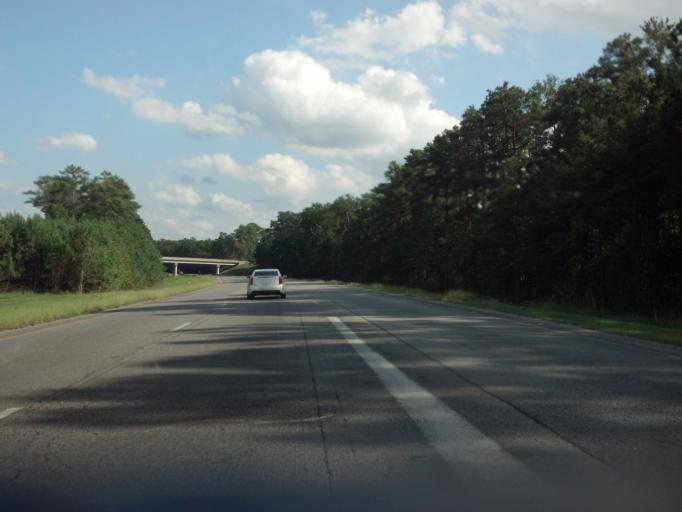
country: US
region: North Carolina
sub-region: Nash County
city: Rocky Mount
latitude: 35.9425
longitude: -77.7579
